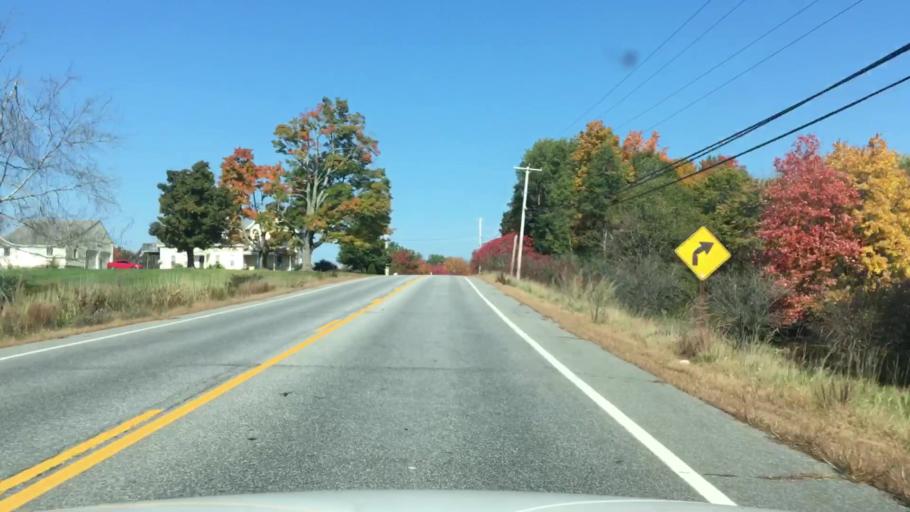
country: US
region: Maine
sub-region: Sagadahoc County
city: Topsham
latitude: 43.9764
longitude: -69.9599
